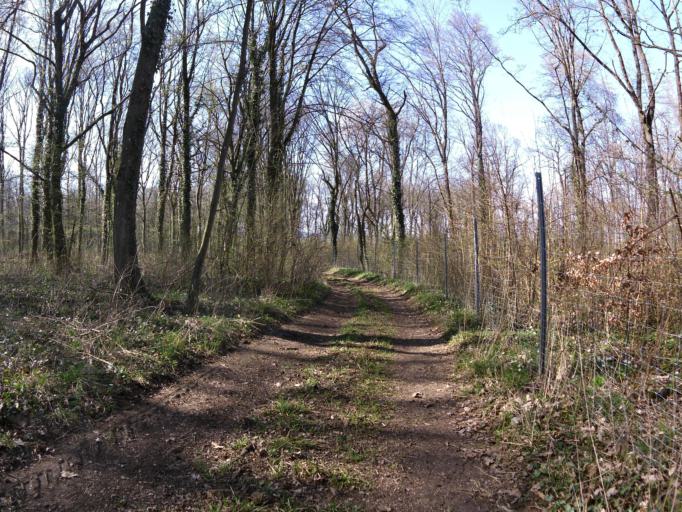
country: DE
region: Bavaria
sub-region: Regierungsbezirk Unterfranken
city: Kurnach
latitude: 49.8312
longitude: 10.0554
